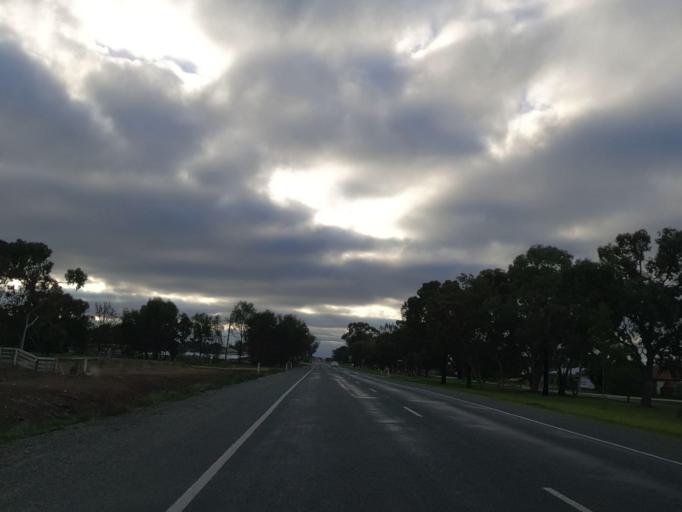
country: AU
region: Victoria
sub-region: Swan Hill
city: Swan Hill
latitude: -35.7434
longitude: 143.9211
